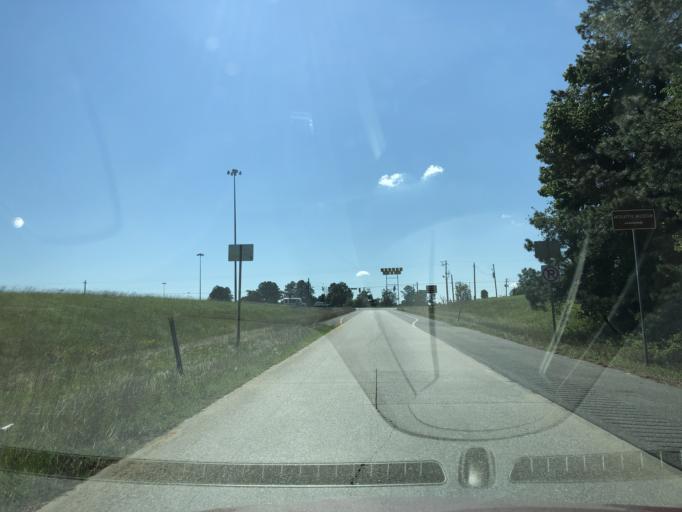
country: US
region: Georgia
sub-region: McDuffie County
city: Thomson
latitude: 33.5105
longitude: -82.5042
